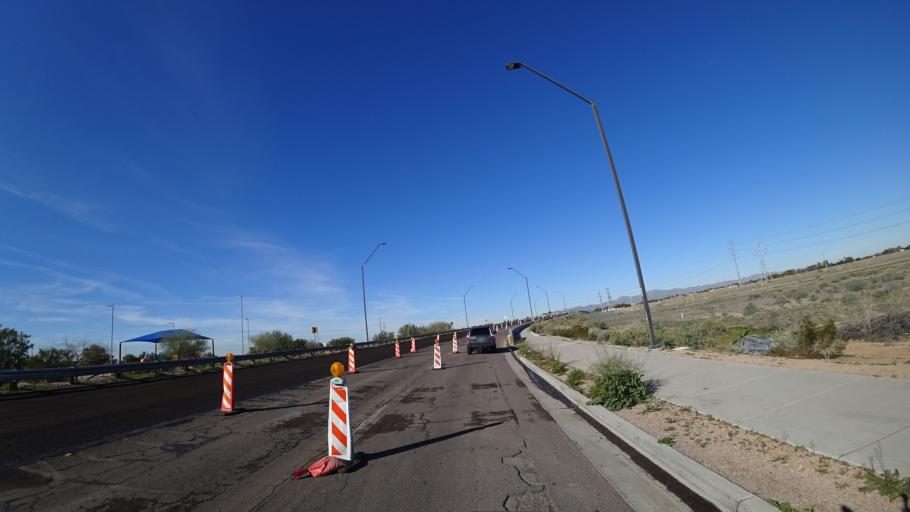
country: US
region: Arizona
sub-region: Maricopa County
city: Avondale
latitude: 33.4615
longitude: -112.3256
